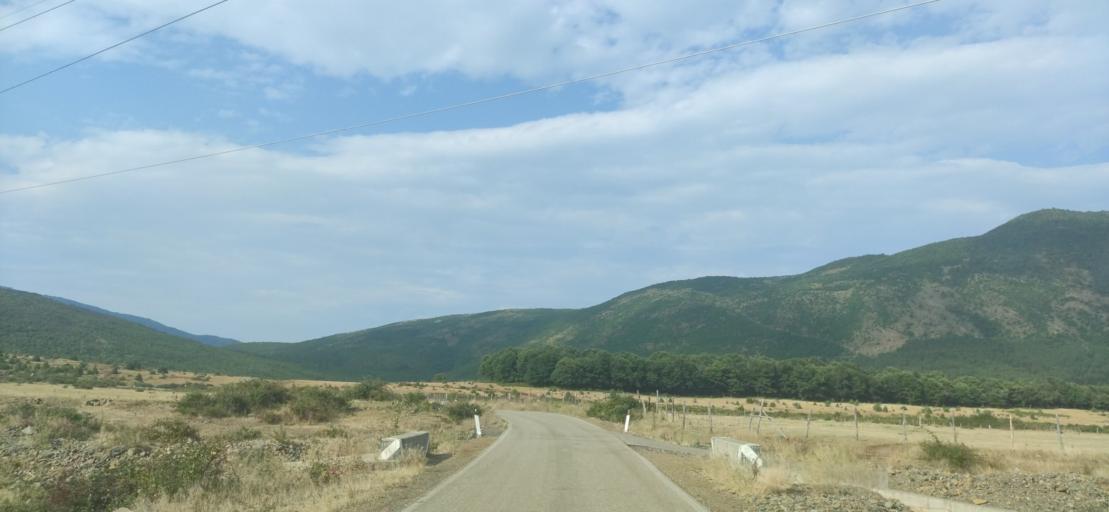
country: AL
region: Shkoder
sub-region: Rrethi i Pukes
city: Iballe
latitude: 42.1855
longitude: 19.9951
